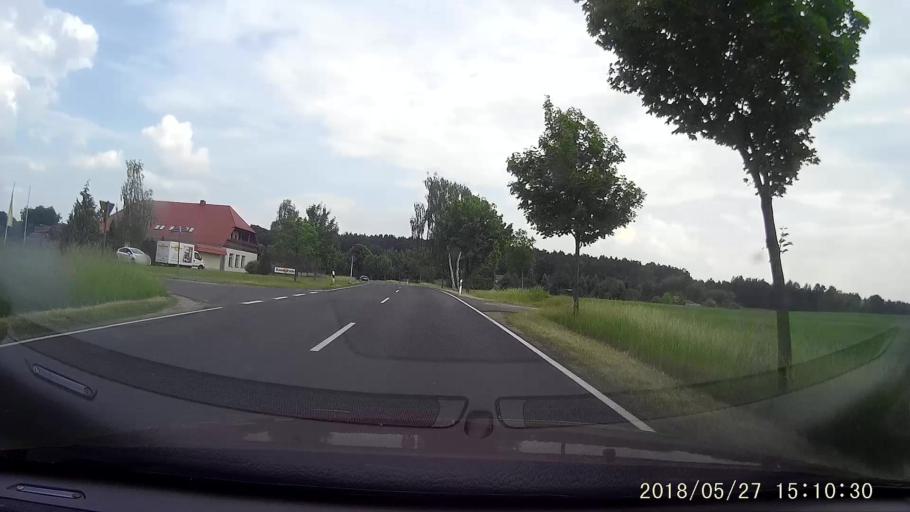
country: DE
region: Saxony
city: Quitzdorf
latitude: 51.2949
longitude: 14.7793
